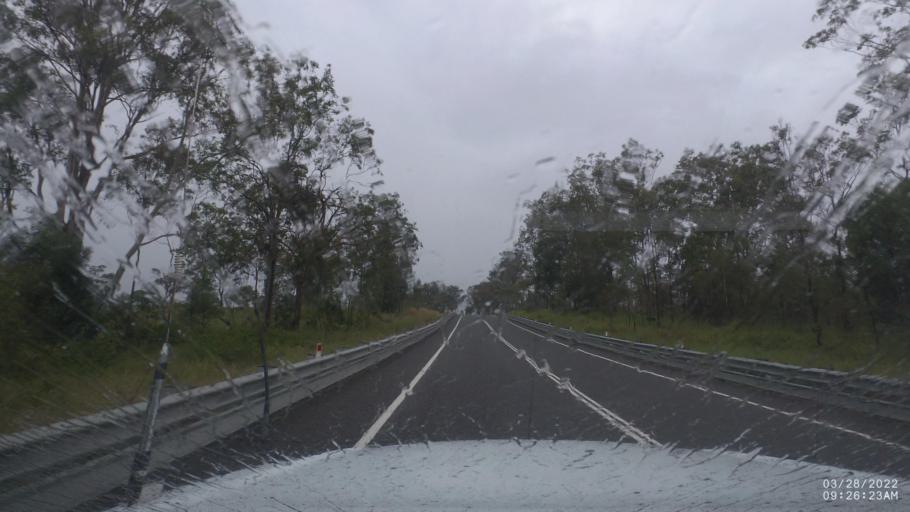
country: AU
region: Queensland
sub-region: Logan
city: Cedar Vale
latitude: -27.9099
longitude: 153.0960
